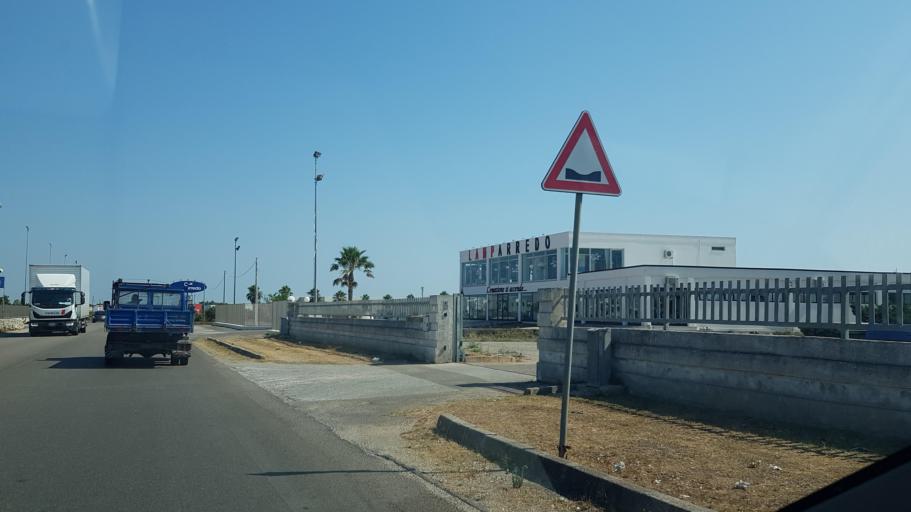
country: IT
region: Apulia
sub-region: Provincia di Lecce
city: Nociglia
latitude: 40.0125
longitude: 18.3242
